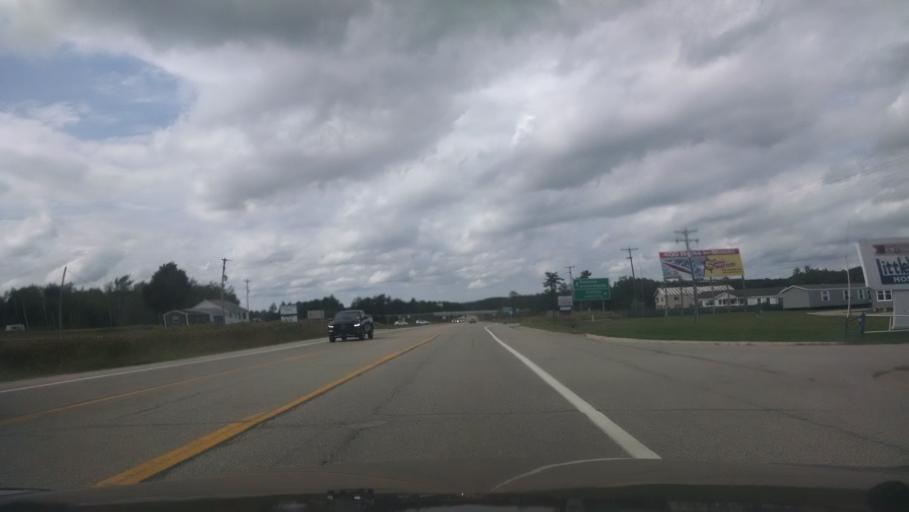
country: US
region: Michigan
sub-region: Wexford County
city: Cadillac
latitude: 44.2025
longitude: -85.4077
